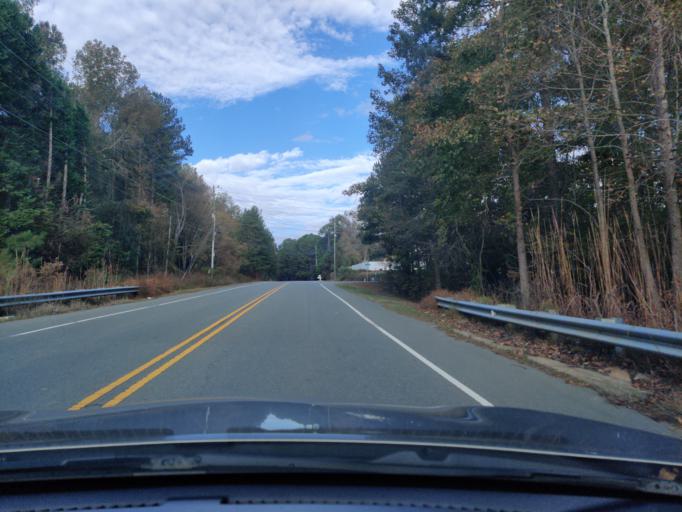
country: US
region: North Carolina
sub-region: Wake County
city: West Raleigh
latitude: 35.9161
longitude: -78.7100
